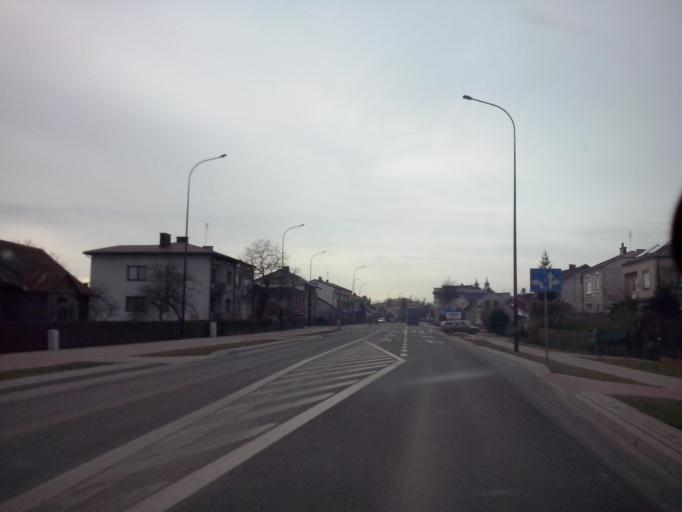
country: PL
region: Lublin Voivodeship
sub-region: Powiat bilgorajski
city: Bilgoraj
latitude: 50.5458
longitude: 22.7320
